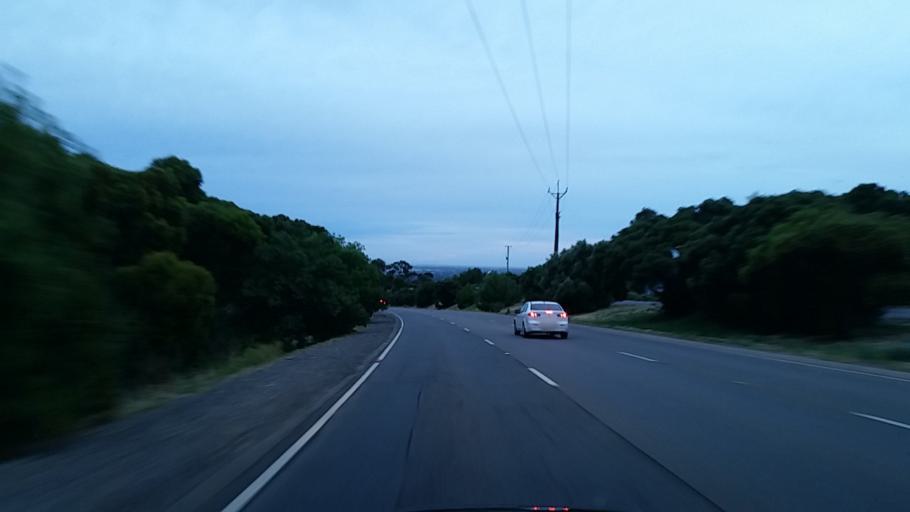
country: AU
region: South Australia
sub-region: Onkaparinga
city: Bedford Park
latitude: -35.0438
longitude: 138.5608
